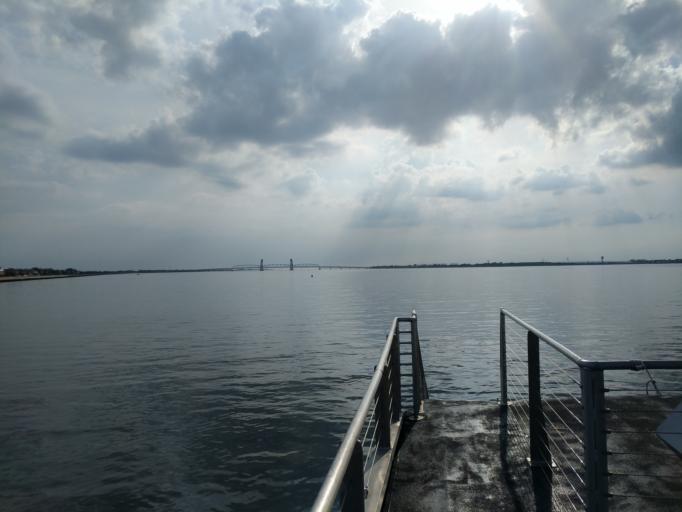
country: US
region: New York
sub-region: Kings County
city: East New York
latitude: 40.5837
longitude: -73.8495
